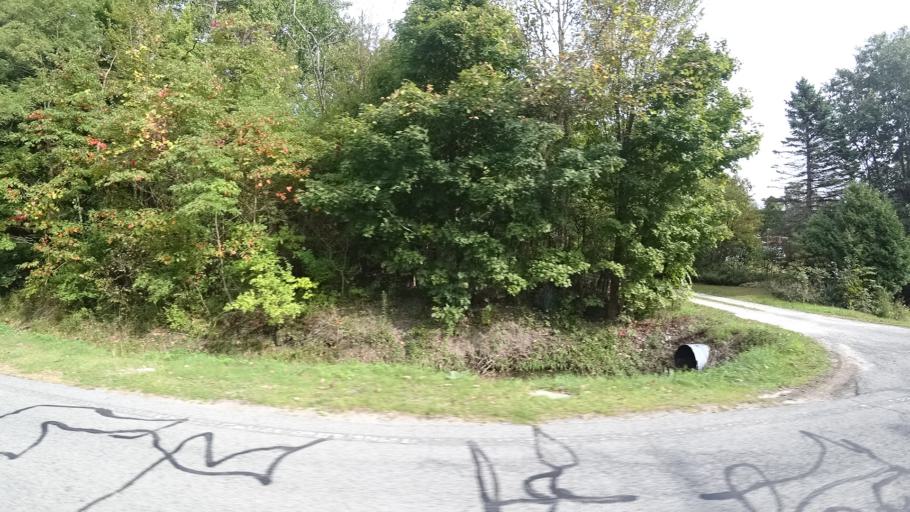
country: US
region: Indiana
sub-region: LaPorte County
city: Long Beach
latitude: 41.7278
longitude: -86.8360
